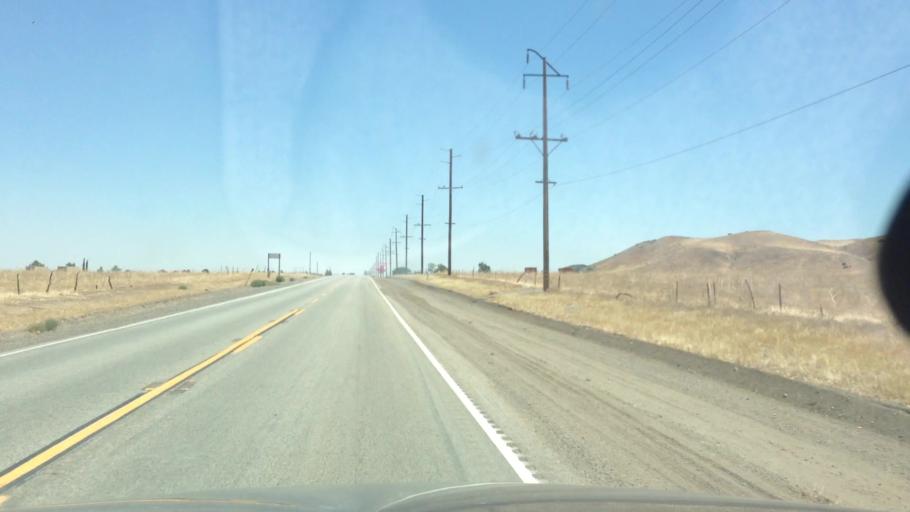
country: US
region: California
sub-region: Kern County
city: Lebec
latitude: 34.7833
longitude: -118.6597
